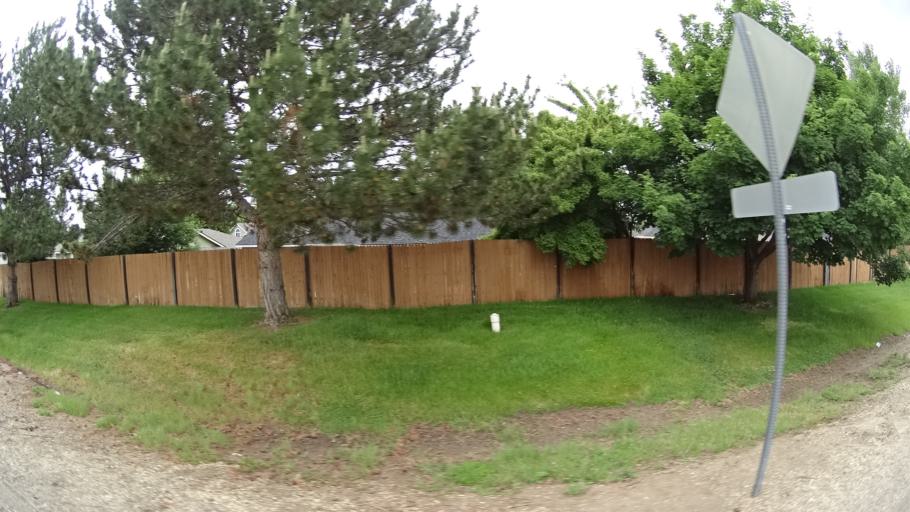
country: US
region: Idaho
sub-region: Ada County
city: Eagle
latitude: 43.7076
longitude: -116.3139
